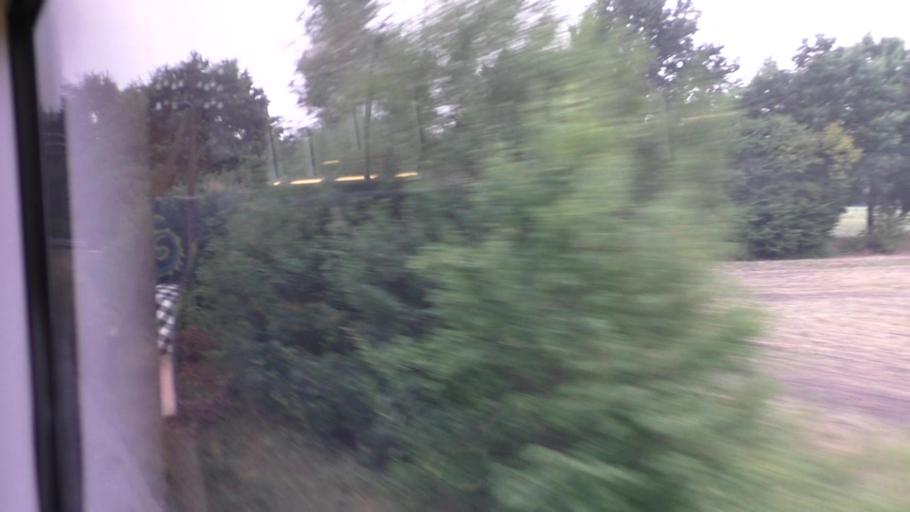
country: DE
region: Saxony
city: Horka
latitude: 51.2806
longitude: 14.9030
